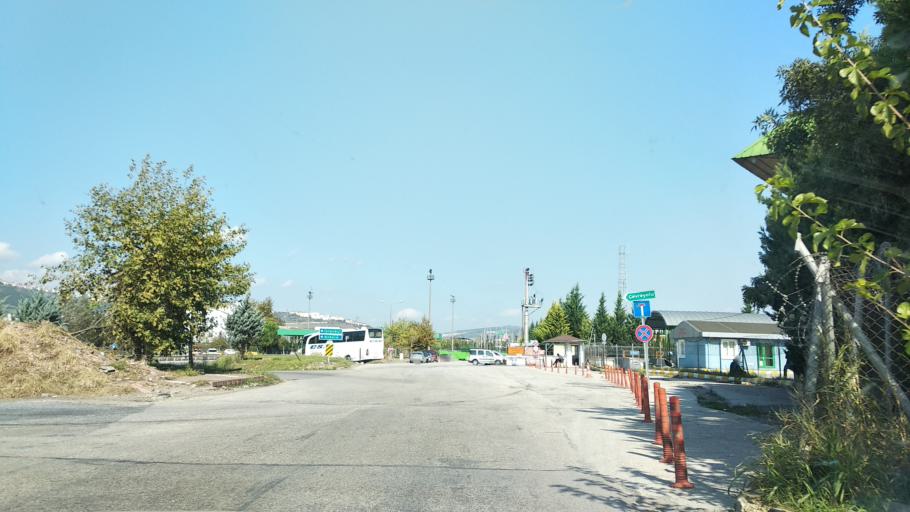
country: TR
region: Kocaeli
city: Kullar
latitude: 40.7765
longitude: 29.9729
